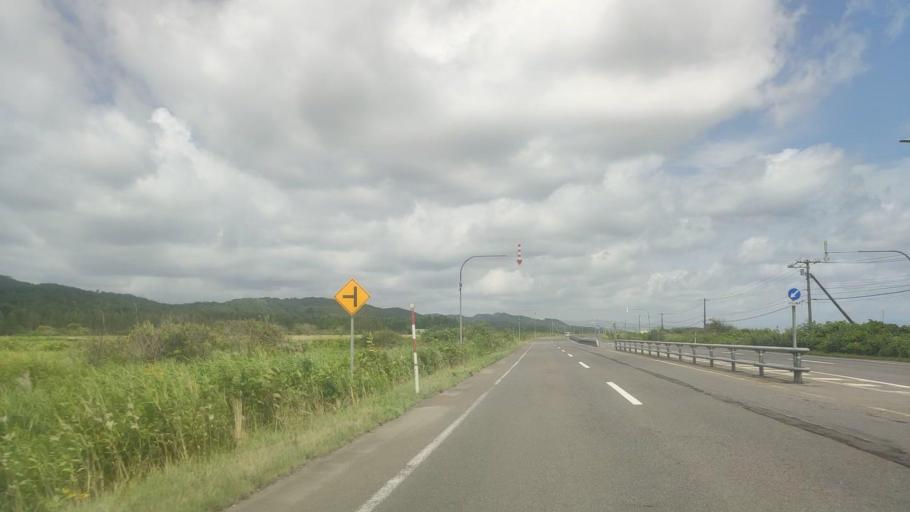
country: JP
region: Hokkaido
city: Niseko Town
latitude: 42.4080
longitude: 140.3059
